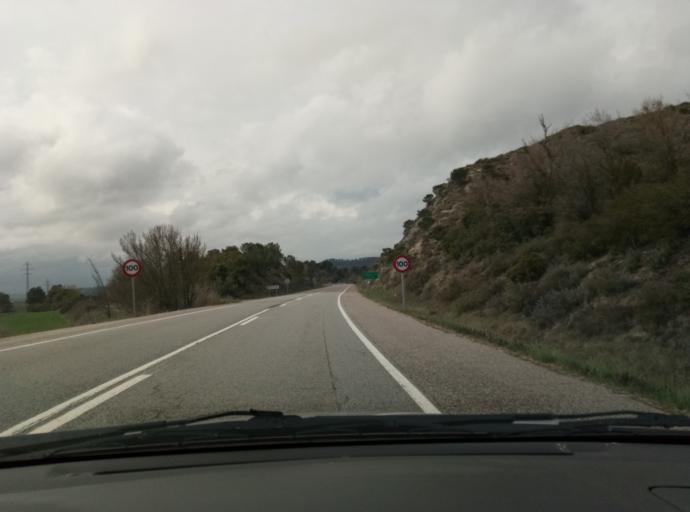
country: ES
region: Catalonia
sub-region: Provincia de Lleida
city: Sant Guim de Freixenet
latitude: 41.6255
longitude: 1.3788
